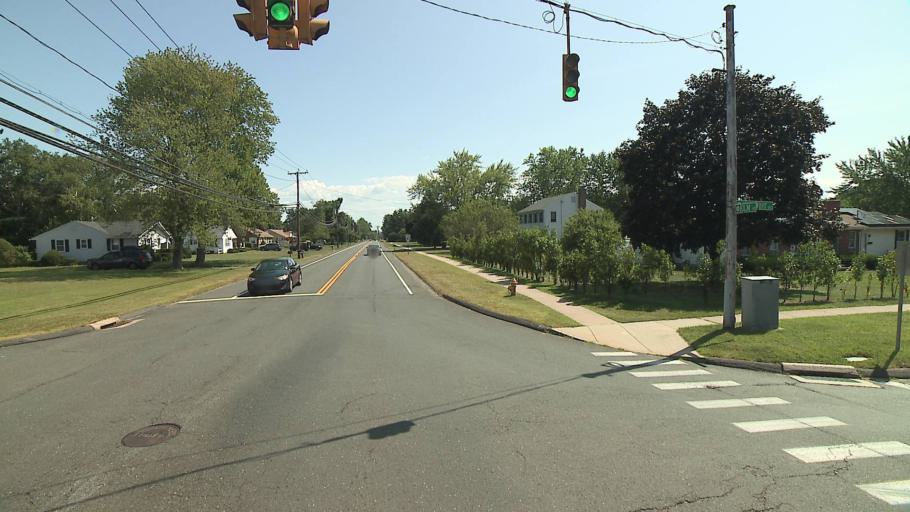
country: US
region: Connecticut
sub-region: Hartford County
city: Windsor Locks
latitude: 41.9265
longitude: -72.6554
